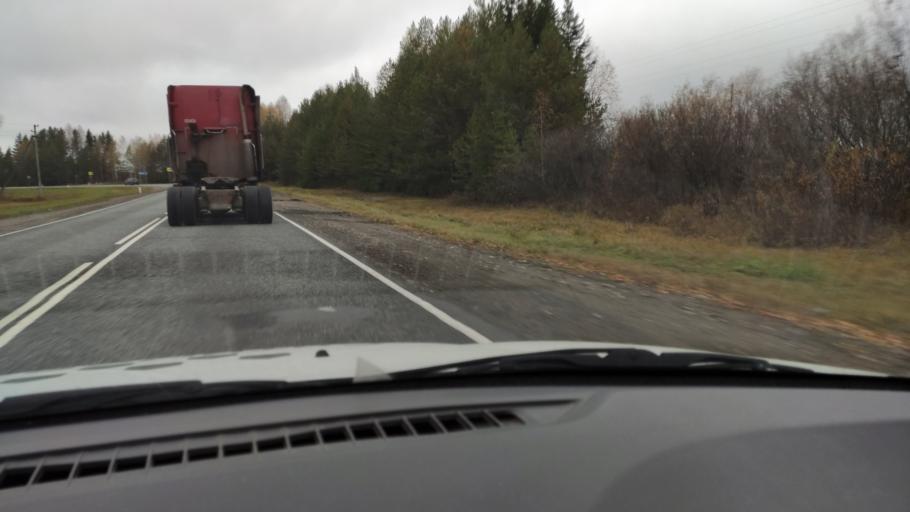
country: RU
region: Kirov
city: Belaya Kholunitsa
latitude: 58.8528
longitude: 50.7306
